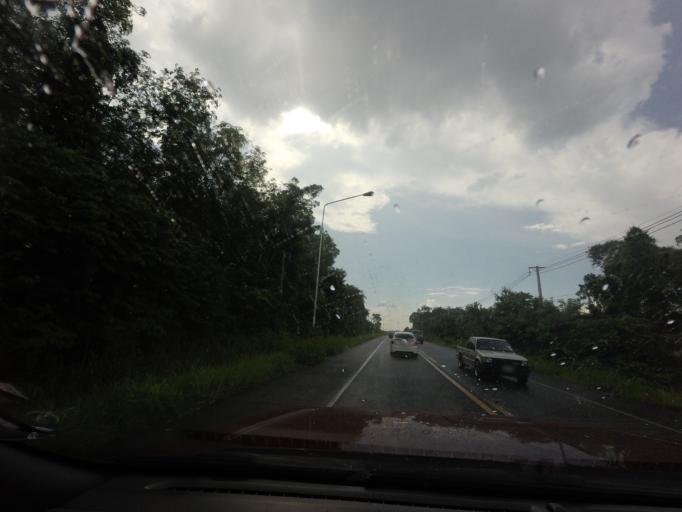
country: TH
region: Pattani
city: Mae Lan
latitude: 6.6562
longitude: 101.1723
